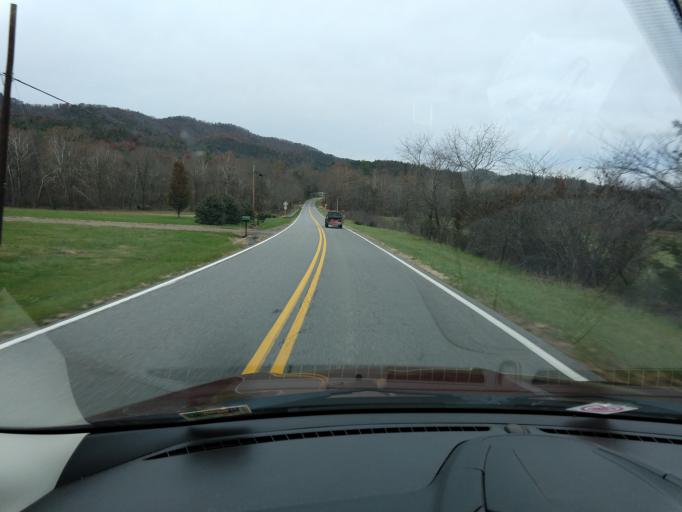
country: US
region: Virginia
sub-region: City of Covington
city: Covington
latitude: 37.7845
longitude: -80.1039
